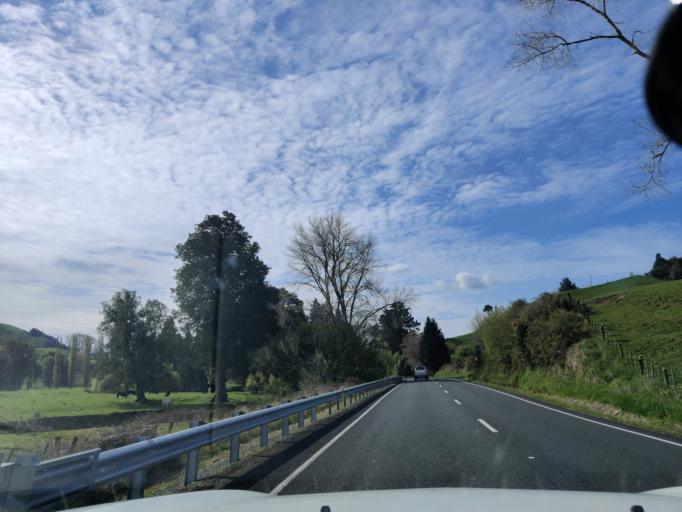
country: NZ
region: Waikato
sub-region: Otorohanga District
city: Otorohanga
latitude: -38.4769
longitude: 175.1741
